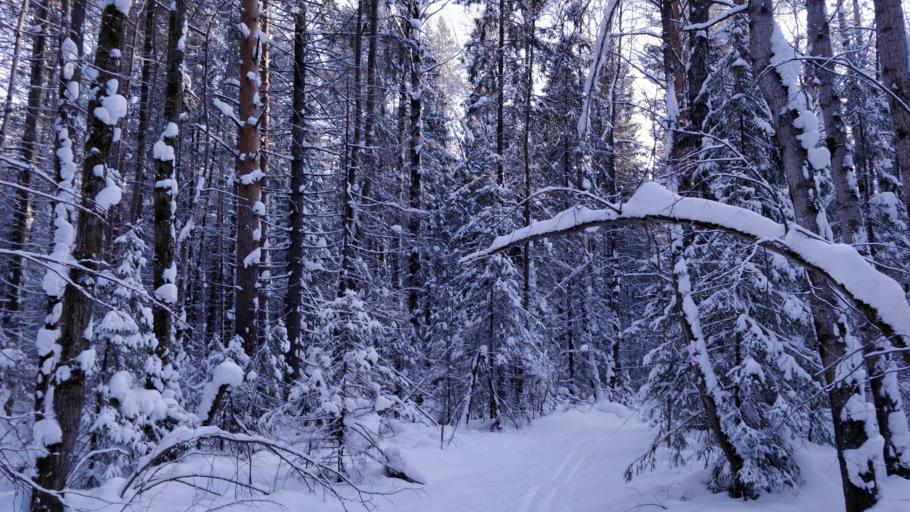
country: RU
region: Perm
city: Perm
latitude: 58.0755
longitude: 56.2117
